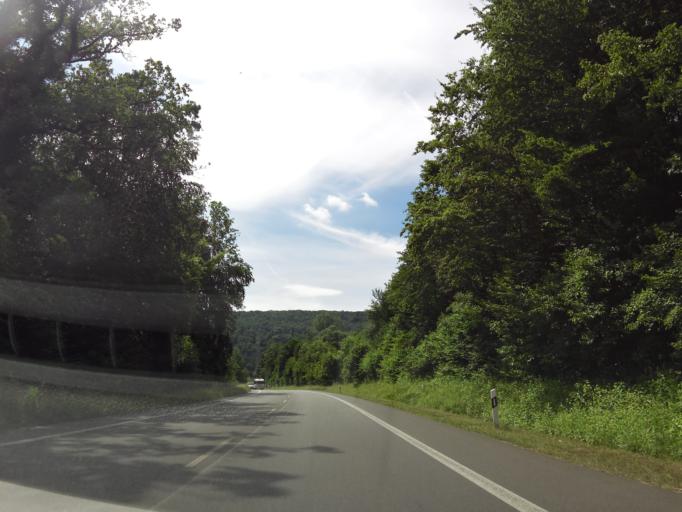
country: DE
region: North Rhine-Westphalia
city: Beverungen
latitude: 51.6459
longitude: 9.3728
